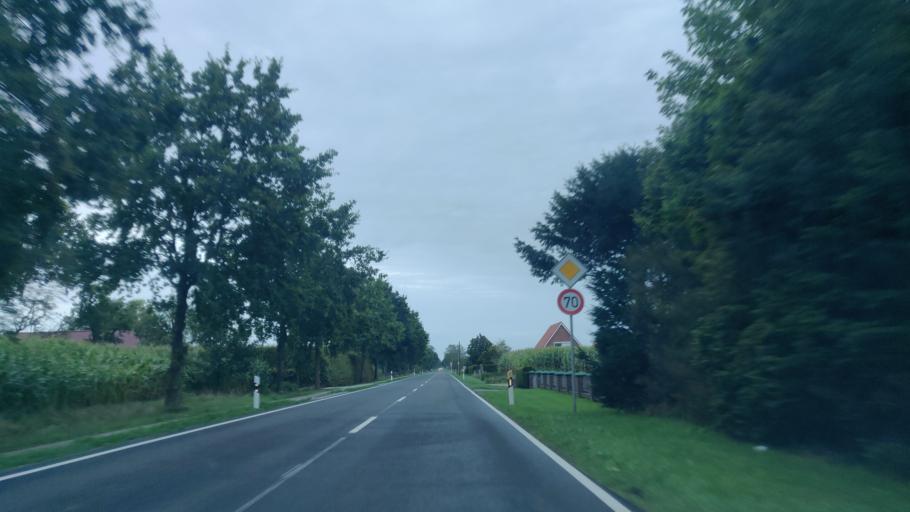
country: DE
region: Lower Saxony
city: Aurich
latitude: 53.4818
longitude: 7.4177
